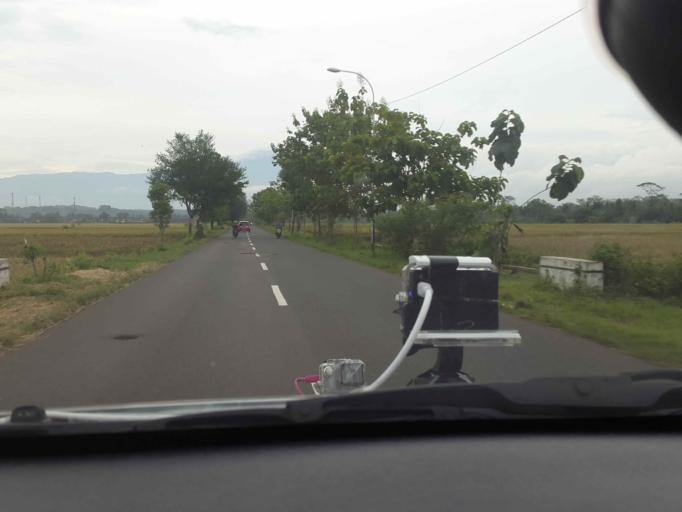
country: ID
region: Central Java
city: Banyumas
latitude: -7.5274
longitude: 109.3046
